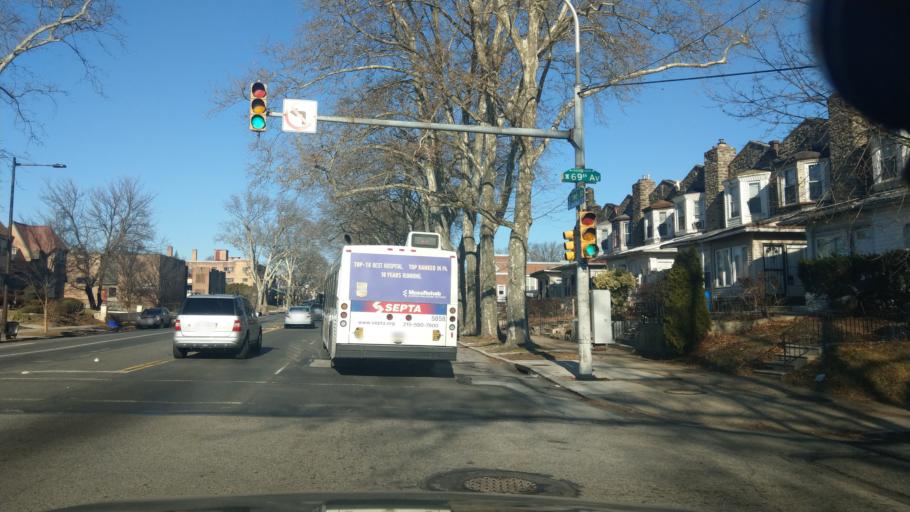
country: US
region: Pennsylvania
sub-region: Montgomery County
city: Wyncote
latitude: 40.0582
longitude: -75.1404
